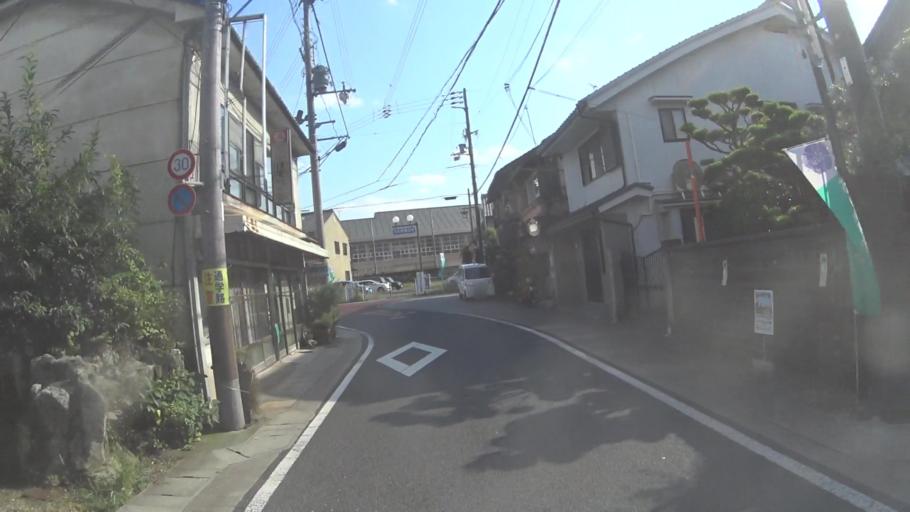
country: JP
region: Kyoto
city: Kameoka
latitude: 35.0132
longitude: 135.5787
